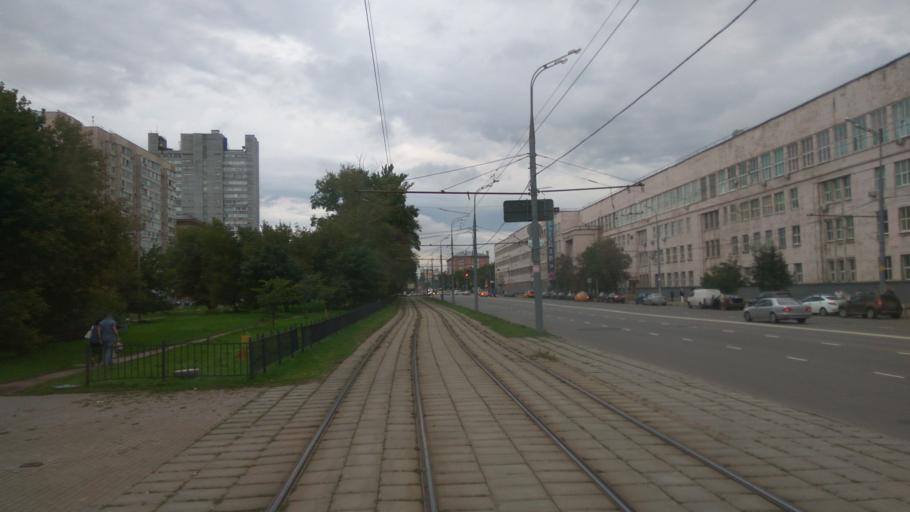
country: RU
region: Moscow
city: Taganskiy
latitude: 55.7183
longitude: 37.6761
